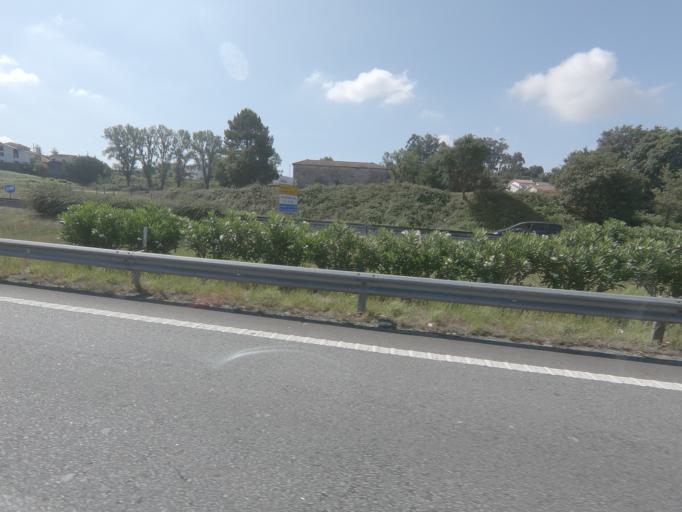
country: PT
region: Porto
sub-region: Maia
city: Pedroucos
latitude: 41.1992
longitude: -8.5813
